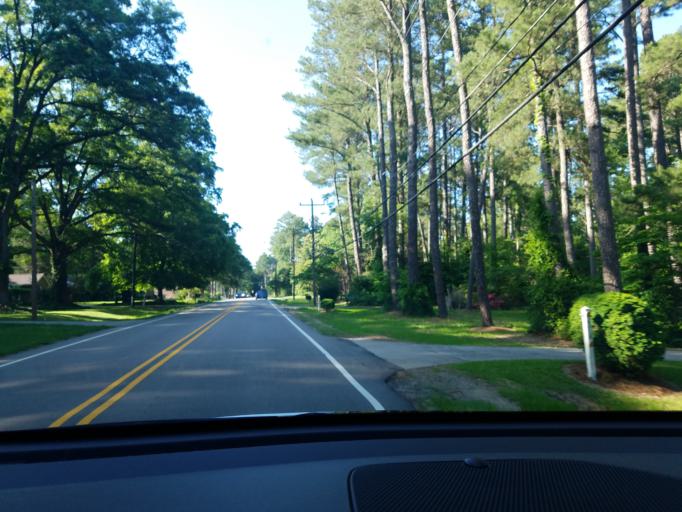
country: US
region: North Carolina
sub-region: Durham County
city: Durham
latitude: 35.9674
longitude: -78.9325
